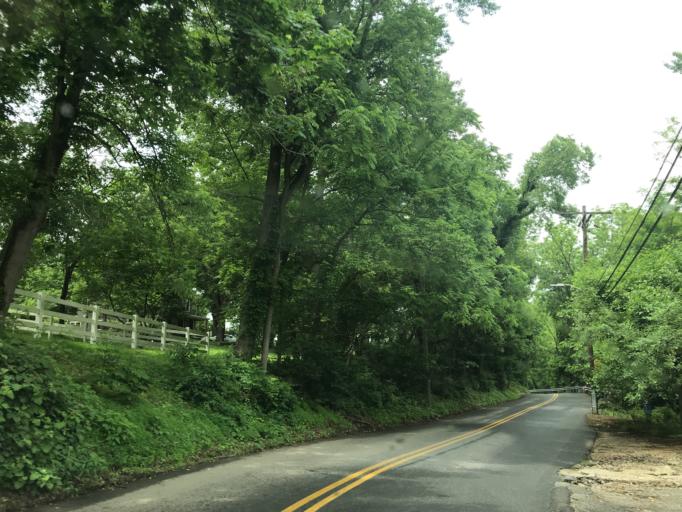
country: US
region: Maryland
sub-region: Howard County
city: Ellicott City
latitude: 39.2755
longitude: -76.7829
